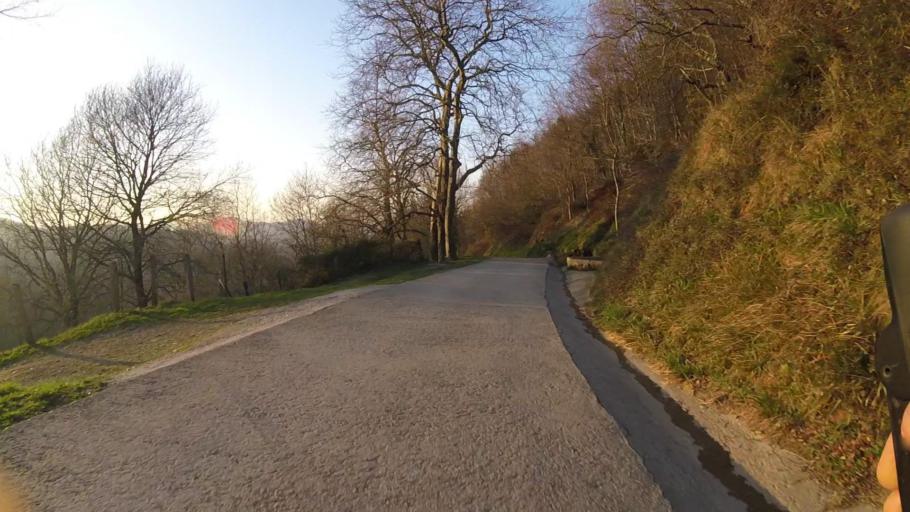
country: ES
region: Basque Country
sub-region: Provincia de Guipuzcoa
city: Errenteria
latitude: 43.2722
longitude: -1.8592
